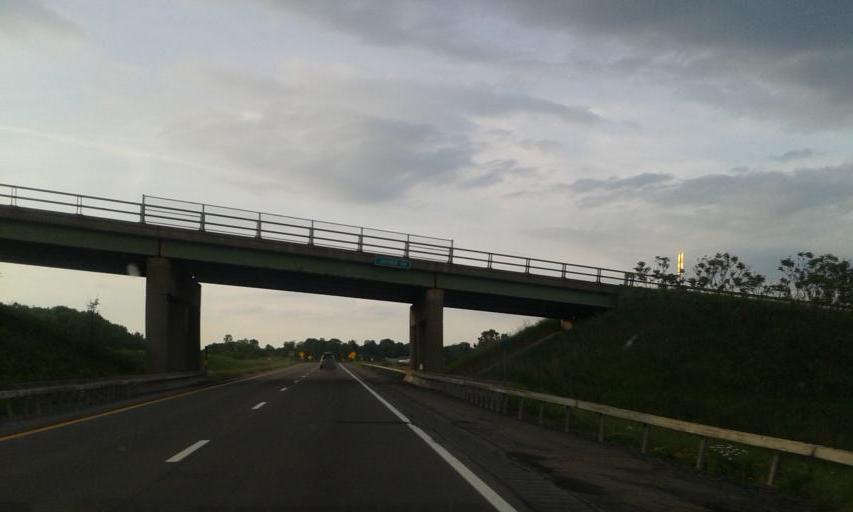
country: US
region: New York
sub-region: Broome County
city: Chenango Bridge
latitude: 42.2864
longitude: -75.9249
